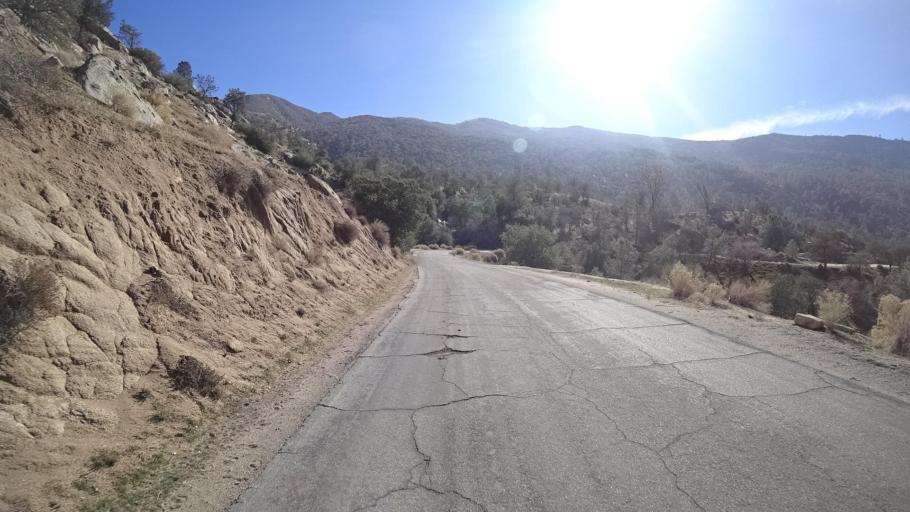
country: US
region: California
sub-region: Kern County
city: Bodfish
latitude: 35.5582
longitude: -118.5786
